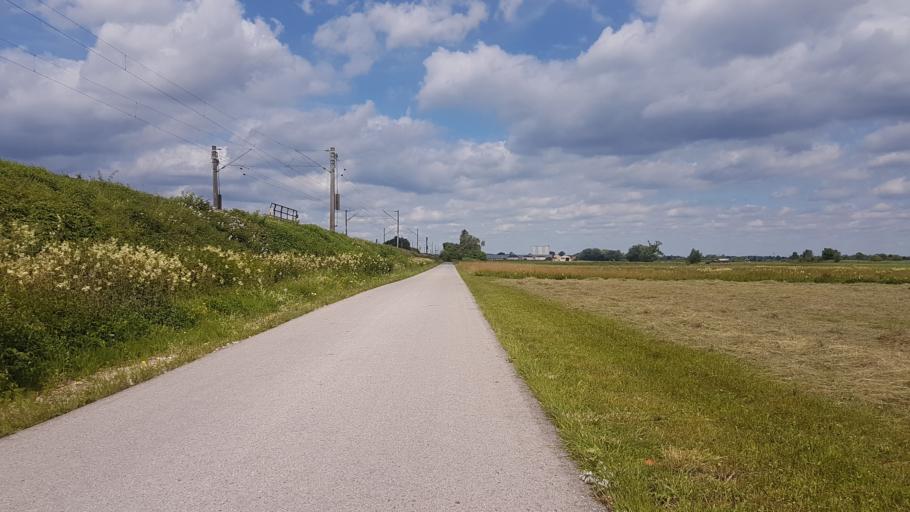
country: DE
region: Bavaria
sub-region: Regierungsbezirk Mittelfranken
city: Gunzenhausen
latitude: 49.0853
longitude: 10.7709
